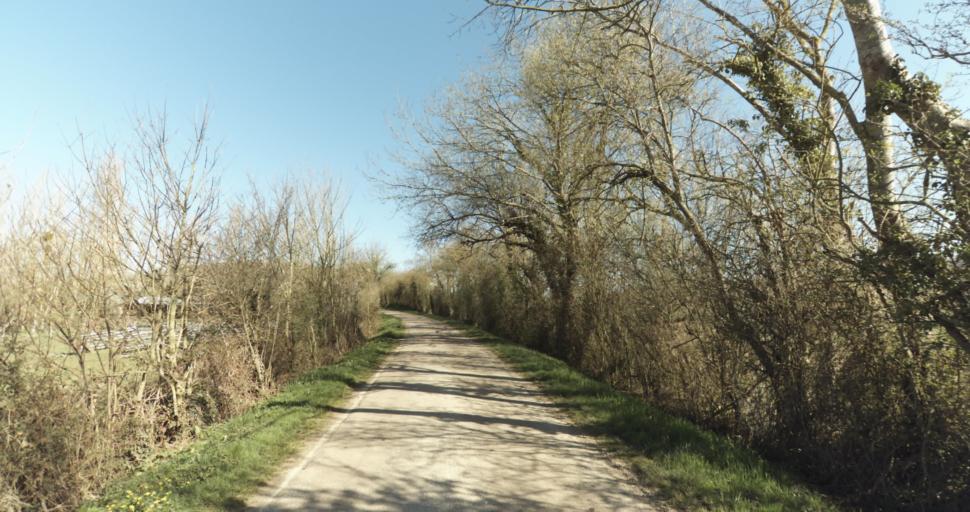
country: FR
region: Lower Normandy
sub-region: Departement du Calvados
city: Saint-Pierre-sur-Dives
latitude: 48.9708
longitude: 0.0525
